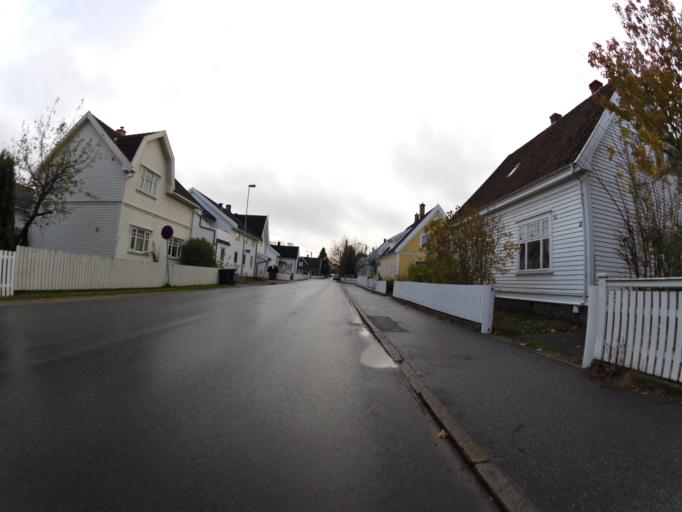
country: NO
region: Ostfold
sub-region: Fredrikstad
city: Fredrikstad
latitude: 59.2312
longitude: 10.9765
